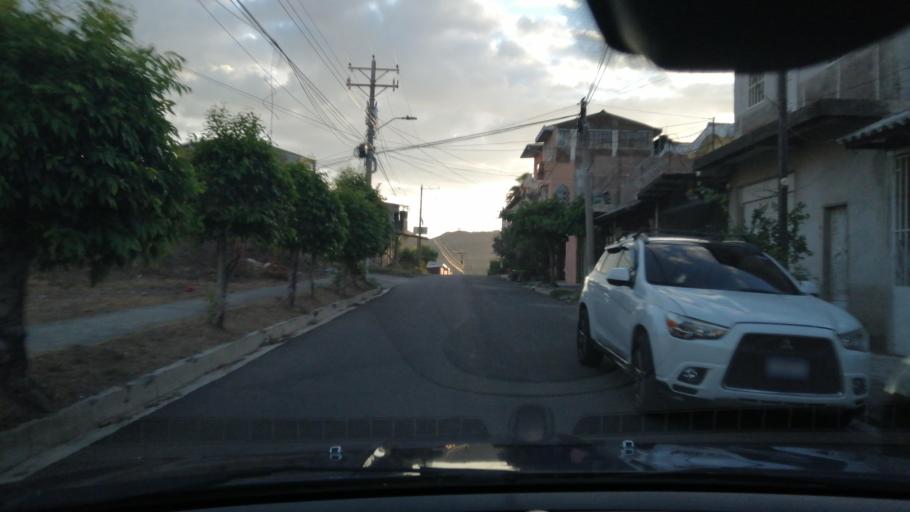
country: SV
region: Santa Ana
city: Metapan
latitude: 14.3295
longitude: -89.4401
